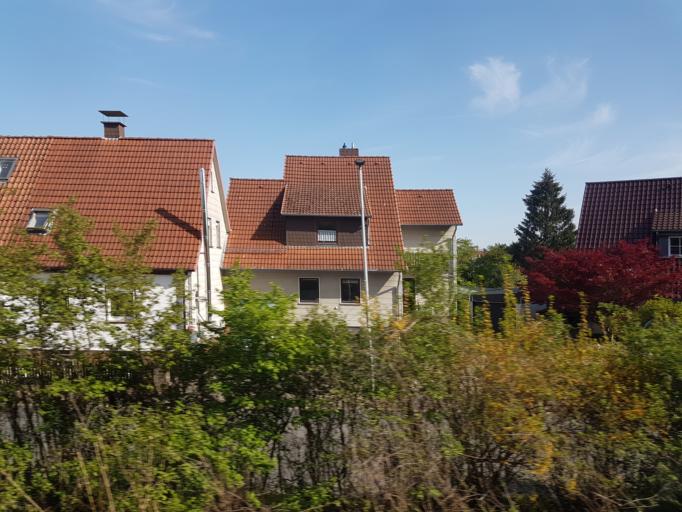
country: DE
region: Lower Saxony
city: Springe
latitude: 52.2127
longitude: 9.5485
